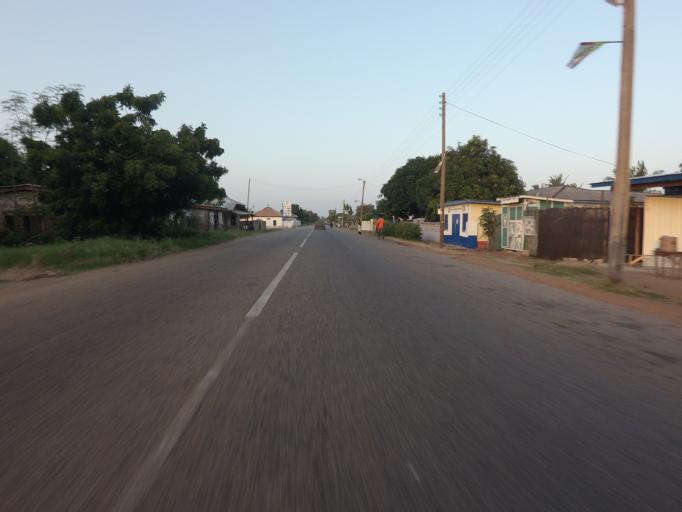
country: GH
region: Volta
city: Anloga
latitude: 5.7986
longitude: 0.9109
